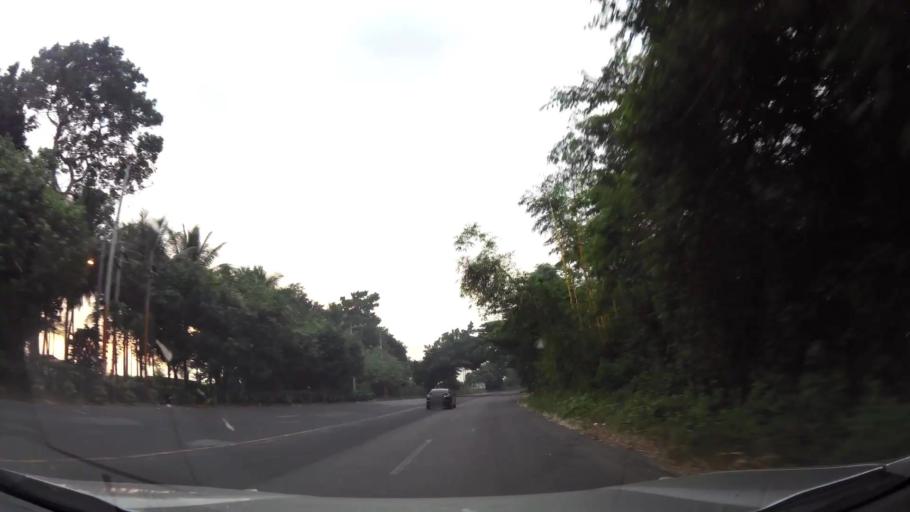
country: GT
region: Escuintla
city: Siquinala
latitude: 14.2837
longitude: -90.9339
